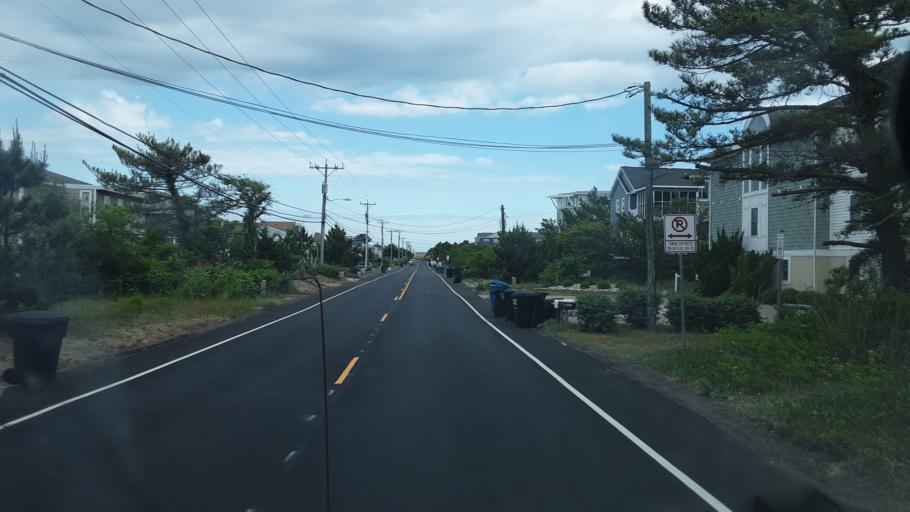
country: US
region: Virginia
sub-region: City of Virginia Beach
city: Virginia Beach
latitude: 36.7277
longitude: -75.9383
